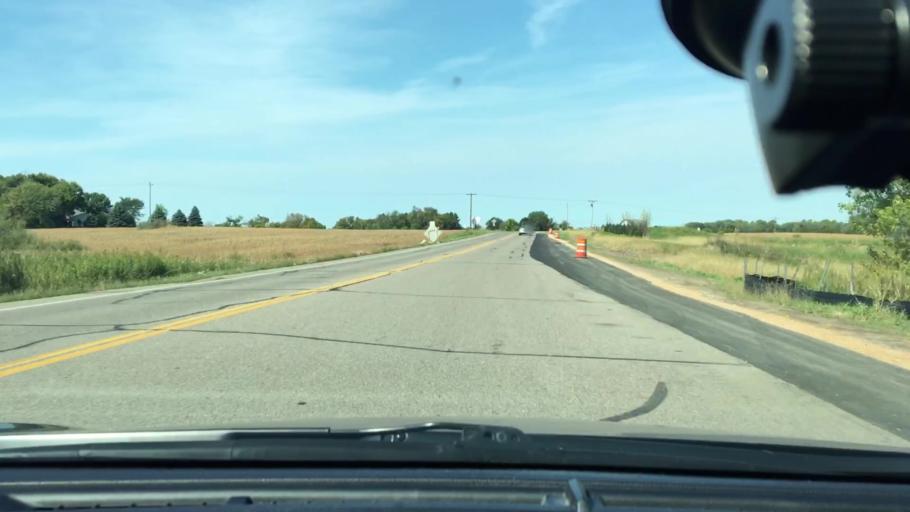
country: US
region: Minnesota
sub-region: Hennepin County
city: Corcoran
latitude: 45.0878
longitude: -93.5306
